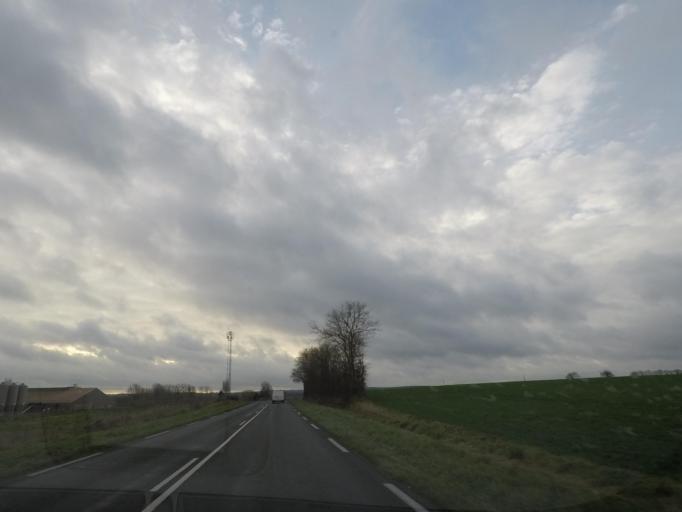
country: FR
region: Pays de la Loire
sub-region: Departement de la Sarthe
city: Vibraye
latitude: 48.0899
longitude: 0.7229
